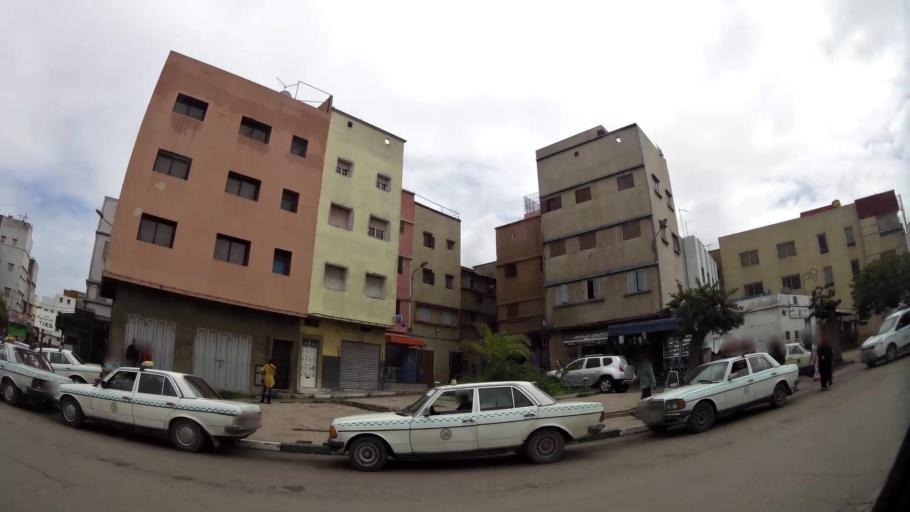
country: MA
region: Grand Casablanca
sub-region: Mediouna
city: Tit Mellil
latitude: 33.6113
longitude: -7.5055
